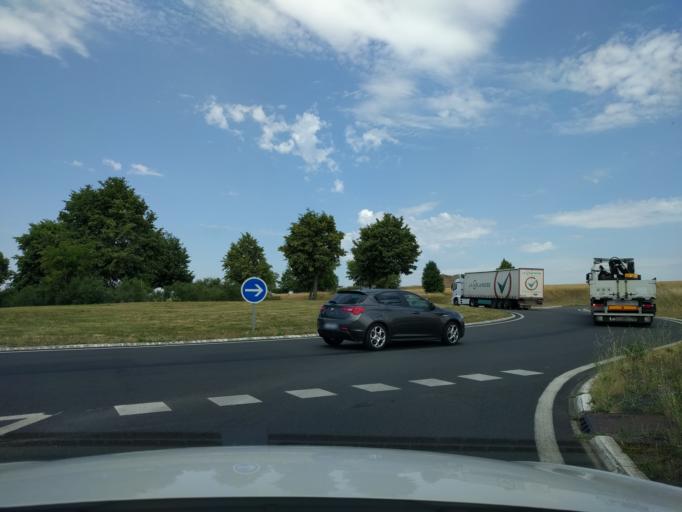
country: FR
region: Poitou-Charentes
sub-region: Departement des Deux-Sevres
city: Bessines
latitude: 46.3488
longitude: -0.5118
